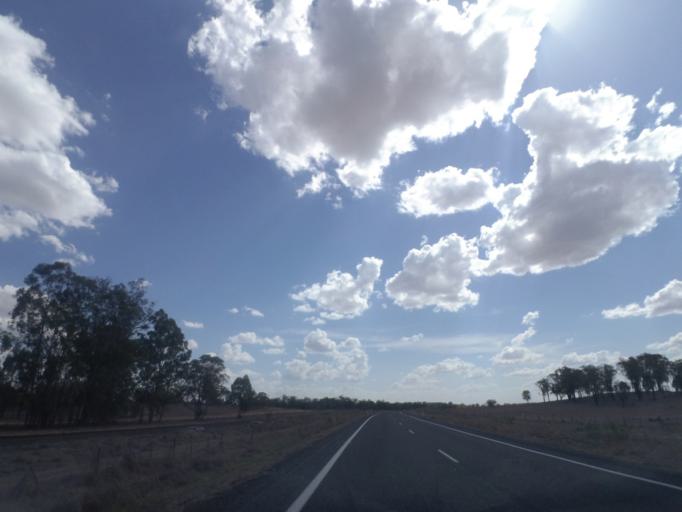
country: AU
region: Queensland
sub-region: Southern Downs
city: Stanthorpe
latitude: -28.3912
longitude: 151.3208
